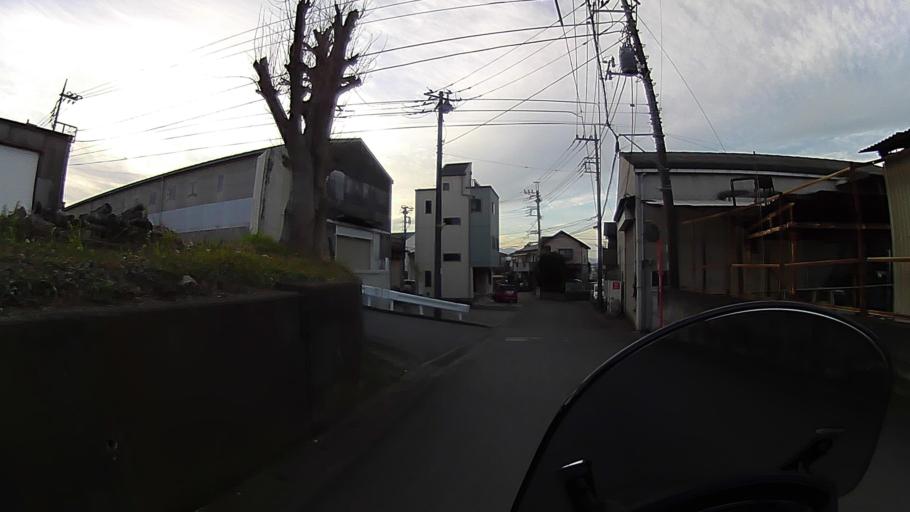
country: JP
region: Kanagawa
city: Atsugi
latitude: 35.4282
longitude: 139.4194
